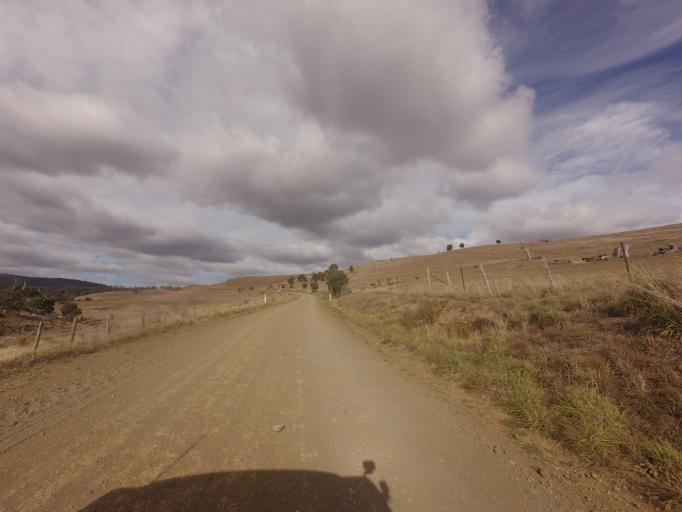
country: AU
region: Tasmania
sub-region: Brighton
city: Bridgewater
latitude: -42.4488
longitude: 147.2346
